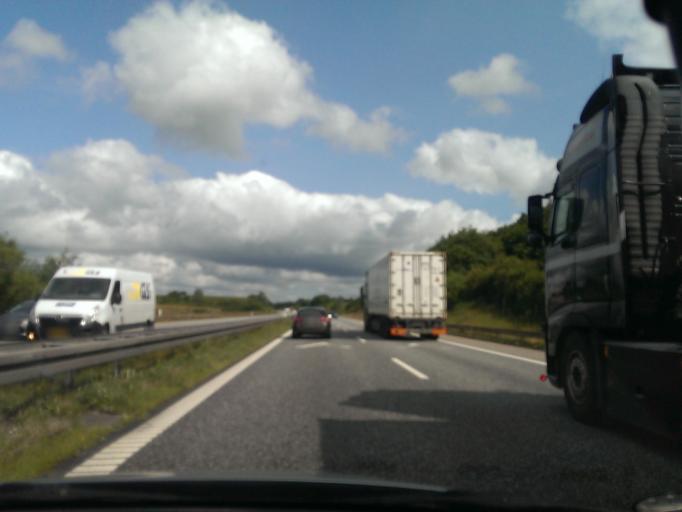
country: DK
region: North Denmark
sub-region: Mariagerfjord Kommune
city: Hobro
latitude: 56.7002
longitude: 9.7293
